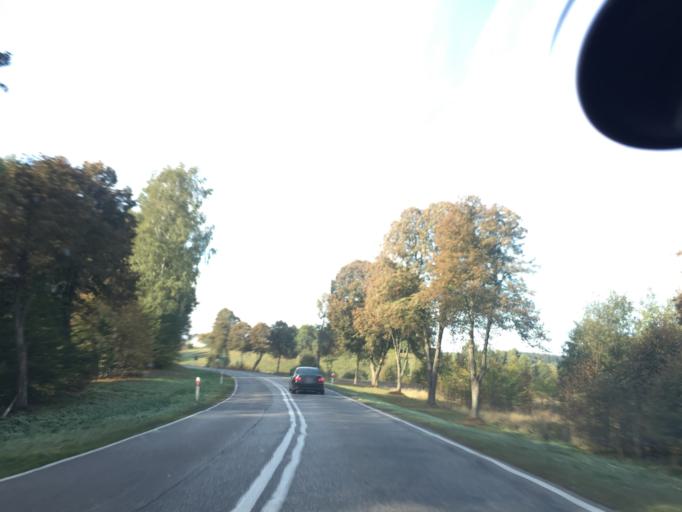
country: PL
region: Warmian-Masurian Voivodeship
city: Dobre Miasto
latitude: 54.0308
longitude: 20.4147
